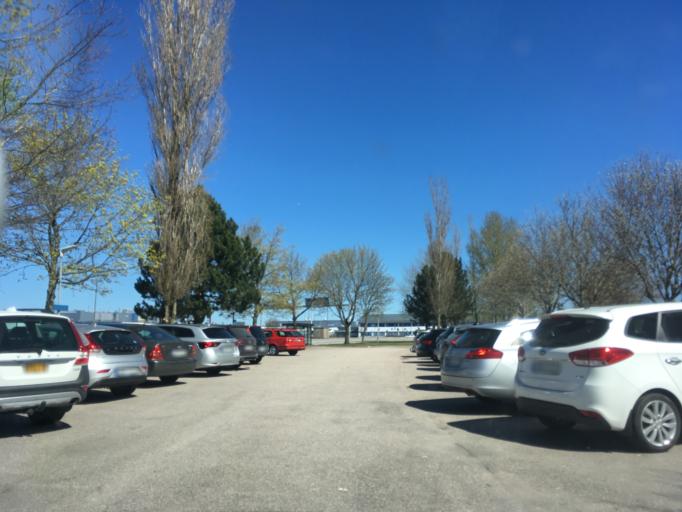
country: SE
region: Vaestra Goetaland
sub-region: Trollhattan
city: Trollhattan
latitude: 58.3100
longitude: 12.3327
